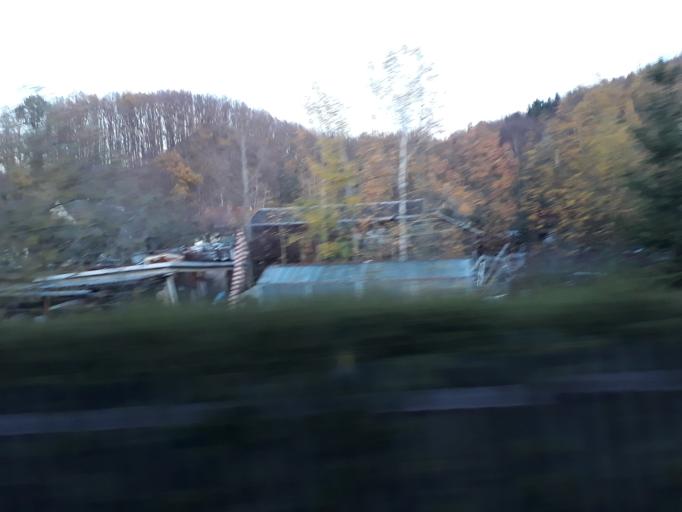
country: DE
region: Saxony
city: Kreischa
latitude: 50.9293
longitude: 13.7775
